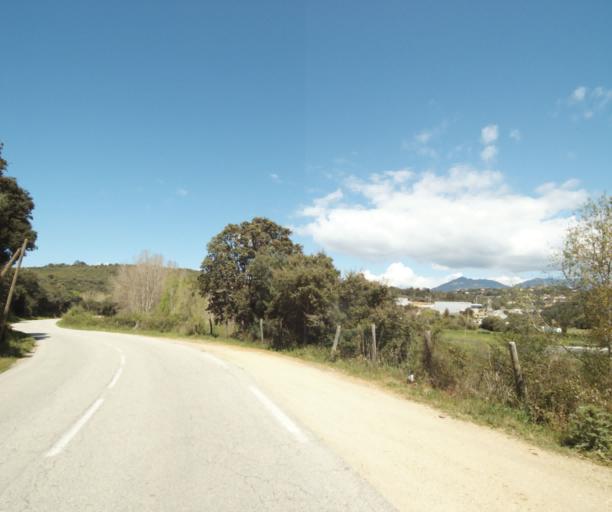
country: FR
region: Corsica
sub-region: Departement de la Corse-du-Sud
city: Propriano
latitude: 41.6579
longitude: 8.9157
